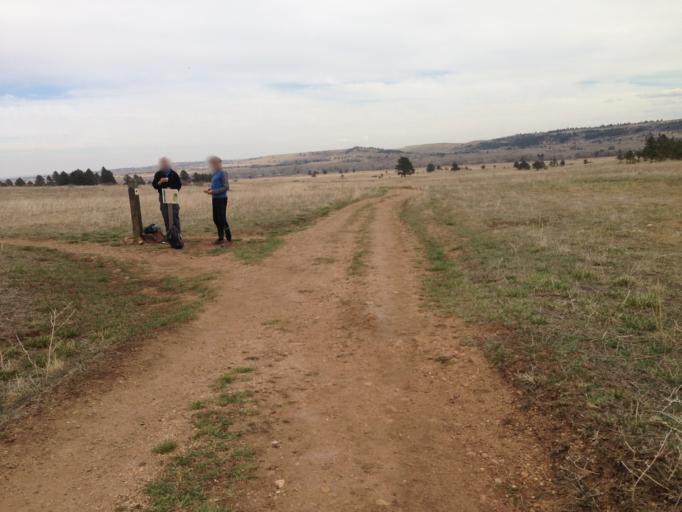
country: US
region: Colorado
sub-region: Boulder County
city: Boulder
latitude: 39.9550
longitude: -105.2605
